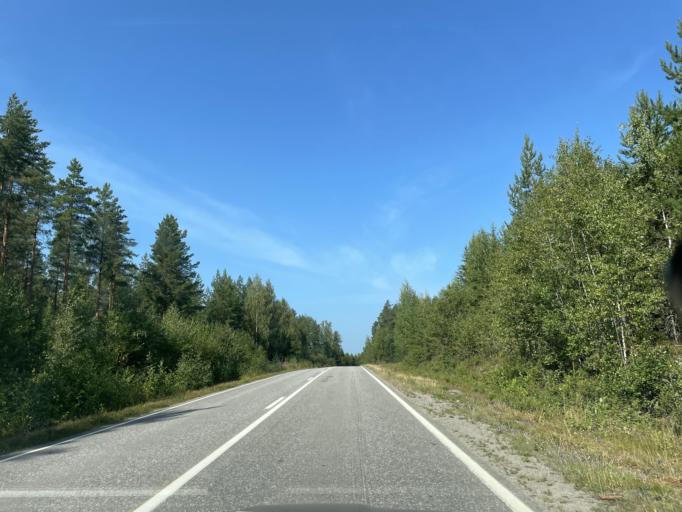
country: FI
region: Central Finland
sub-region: Saarijaervi-Viitasaari
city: Pihtipudas
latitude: 63.3694
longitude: 25.6217
